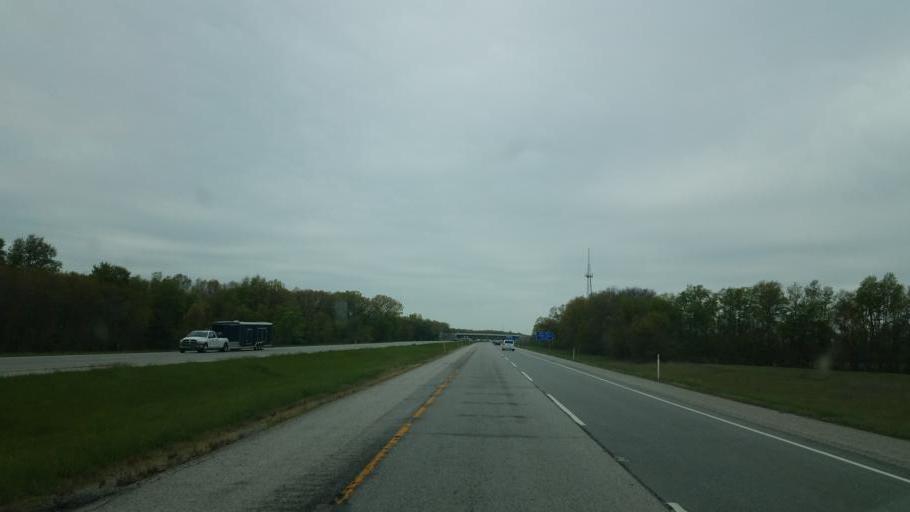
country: US
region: Michigan
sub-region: Saint Joseph County
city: White Pigeon
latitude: 41.7527
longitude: -85.6528
